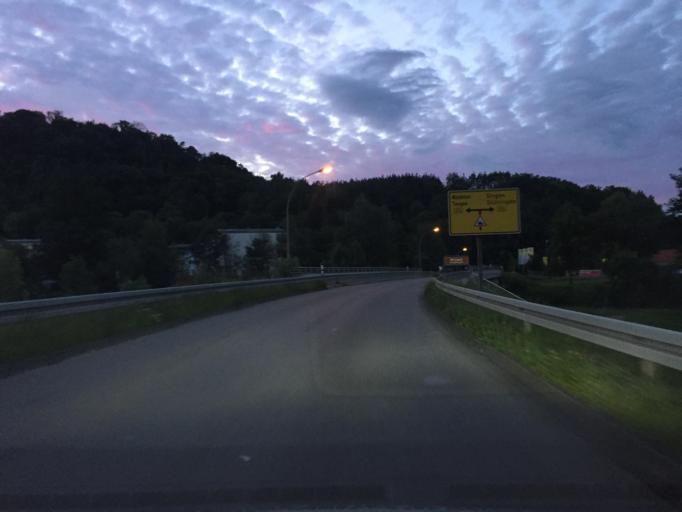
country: DE
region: Baden-Wuerttemberg
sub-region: Freiburg Region
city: Wutoschingen
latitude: 47.6653
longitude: 8.3744
